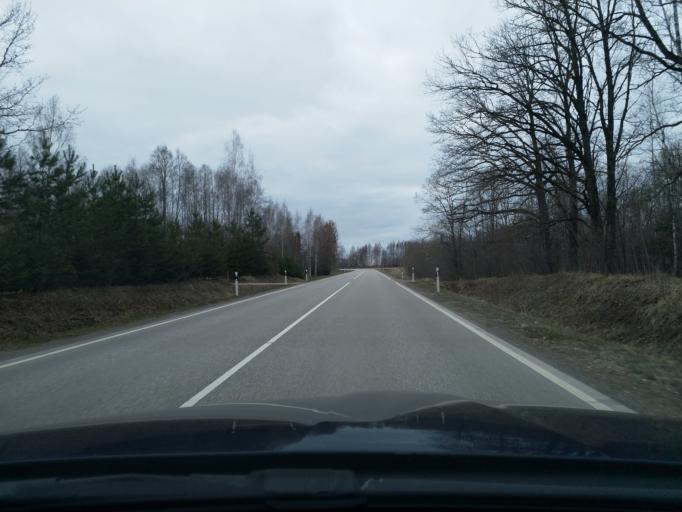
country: LV
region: Talsu Rajons
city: Sabile
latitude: 56.9478
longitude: 22.4775
